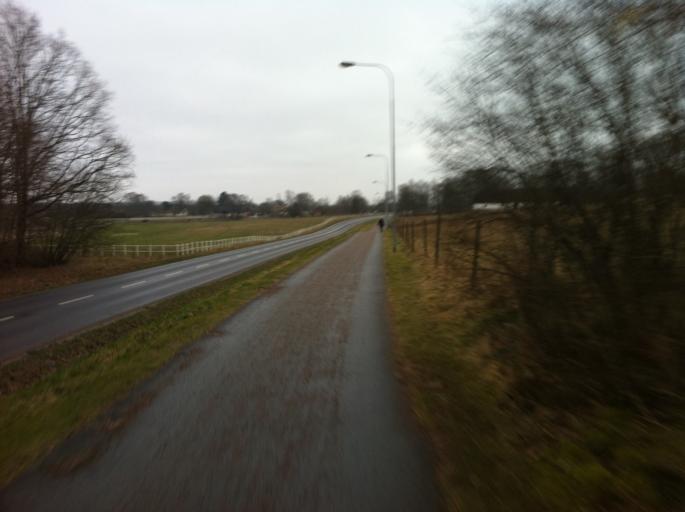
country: SE
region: Skane
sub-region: Hoors Kommun
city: Satofta
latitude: 55.9130
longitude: 13.5491
